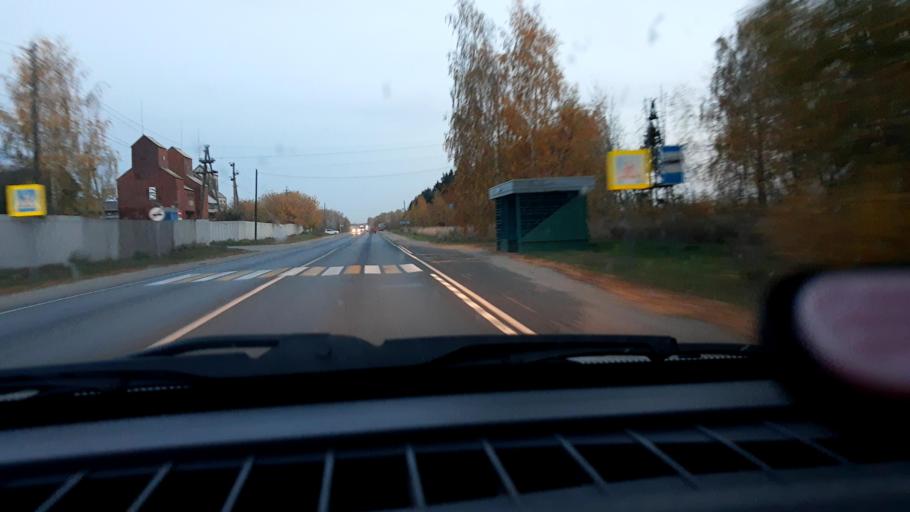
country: RU
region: Nizjnij Novgorod
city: Gorodets
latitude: 56.6364
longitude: 43.5266
